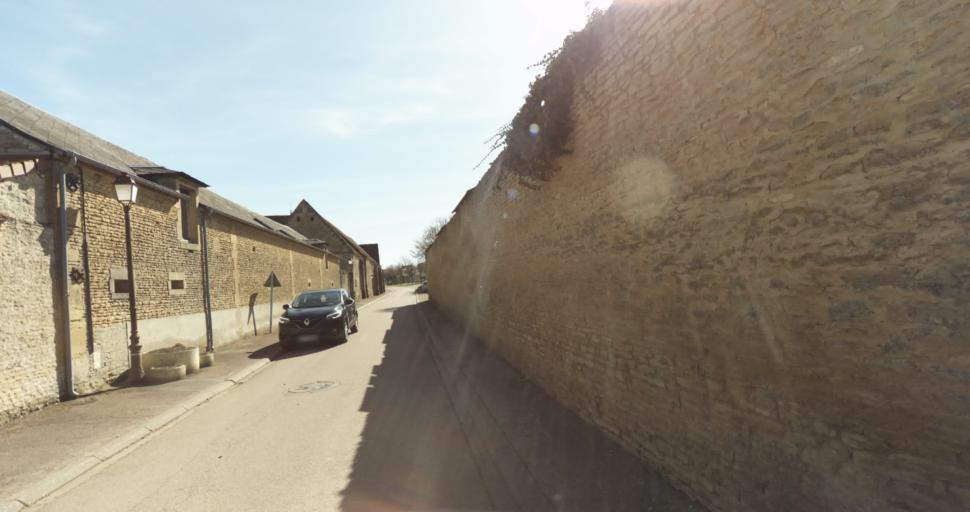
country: FR
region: Lower Normandy
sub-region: Departement du Calvados
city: Saint-Pierre-sur-Dives
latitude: 49.0378
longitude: -0.0263
